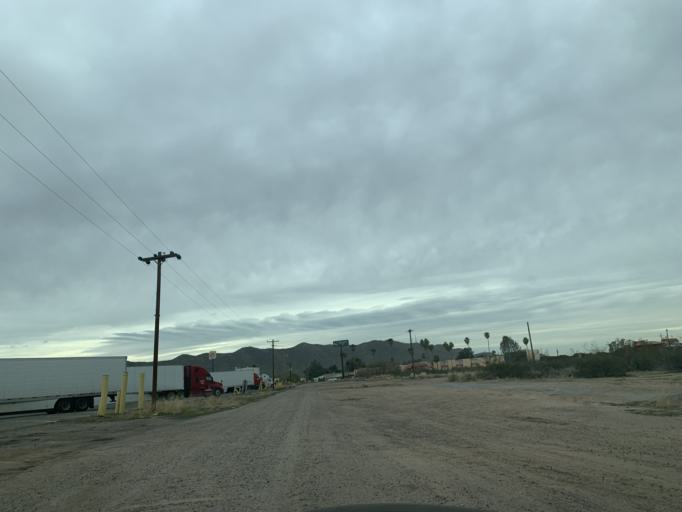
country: US
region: Arizona
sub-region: Pinal County
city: Arizona City
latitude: 32.8139
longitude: -111.6686
